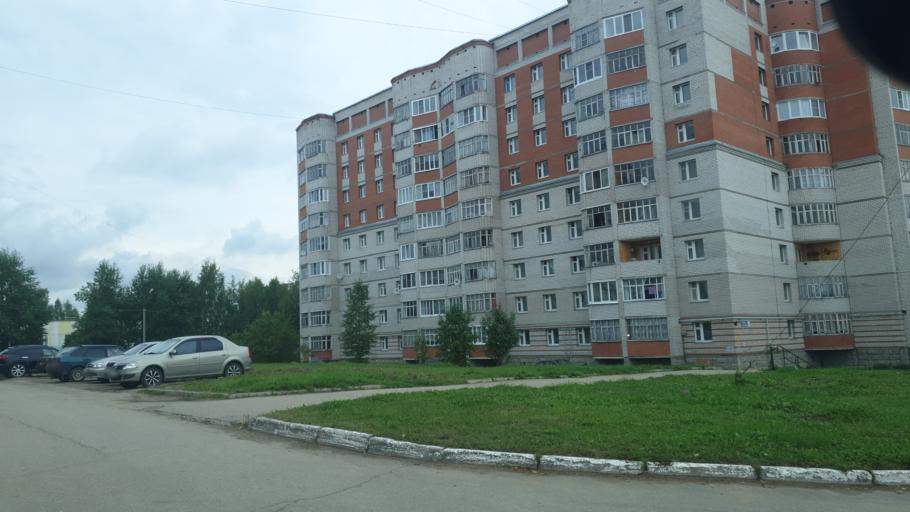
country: RU
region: Komi Republic
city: Ezhva
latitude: 61.7827
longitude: 50.7569
